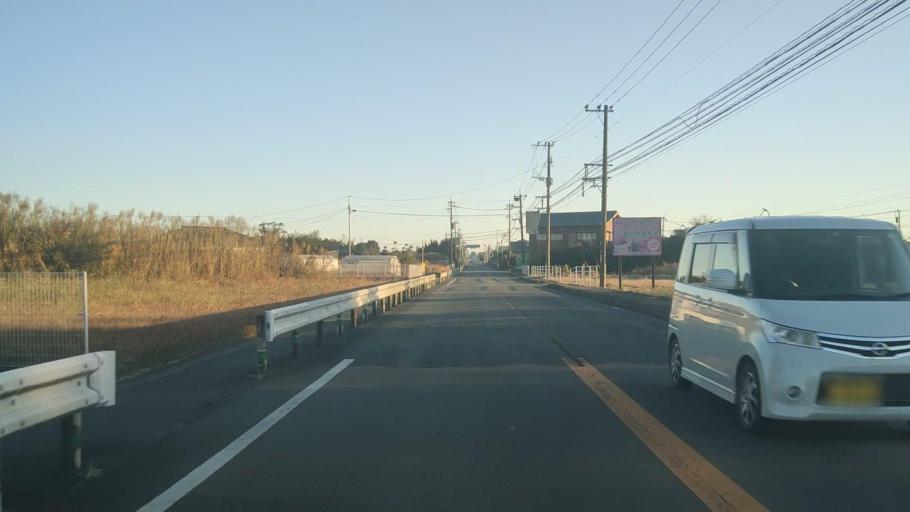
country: JP
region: Miyazaki
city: Miyazaki-shi
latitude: 31.9968
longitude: 131.4635
